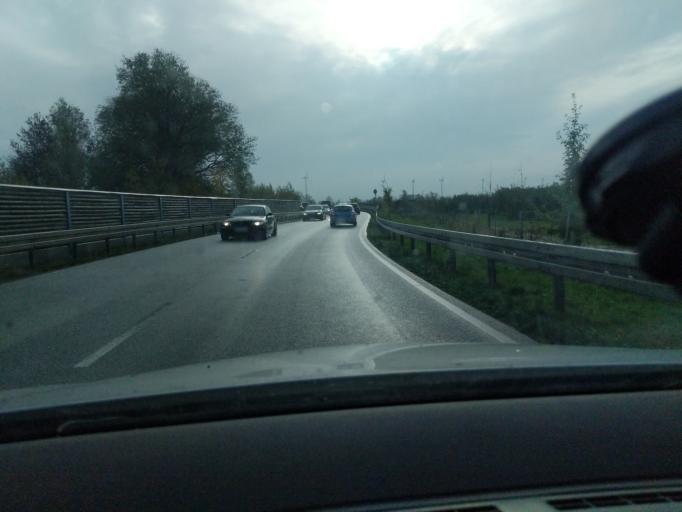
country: DE
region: Lower Saxony
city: Neu Wulmstorf
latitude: 53.5129
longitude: 9.8378
